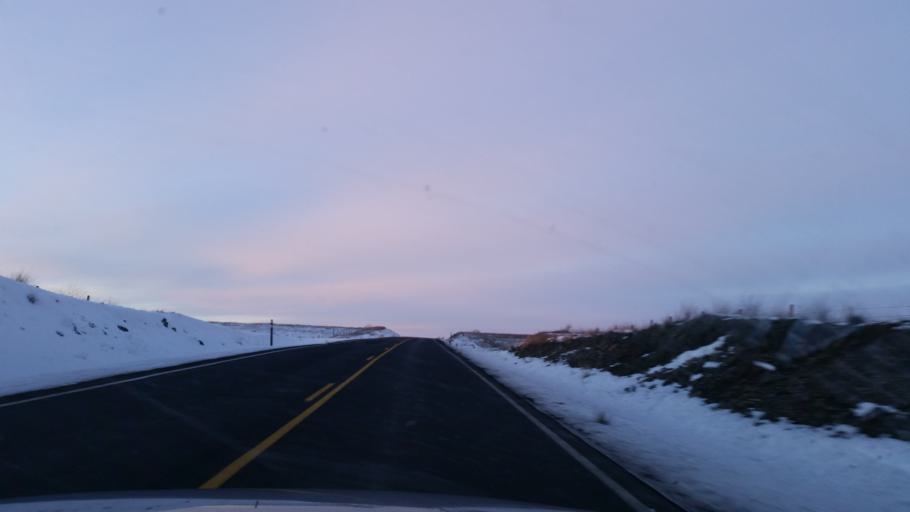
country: US
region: Washington
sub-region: Spokane County
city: Medical Lake
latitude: 47.2329
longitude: -117.9132
